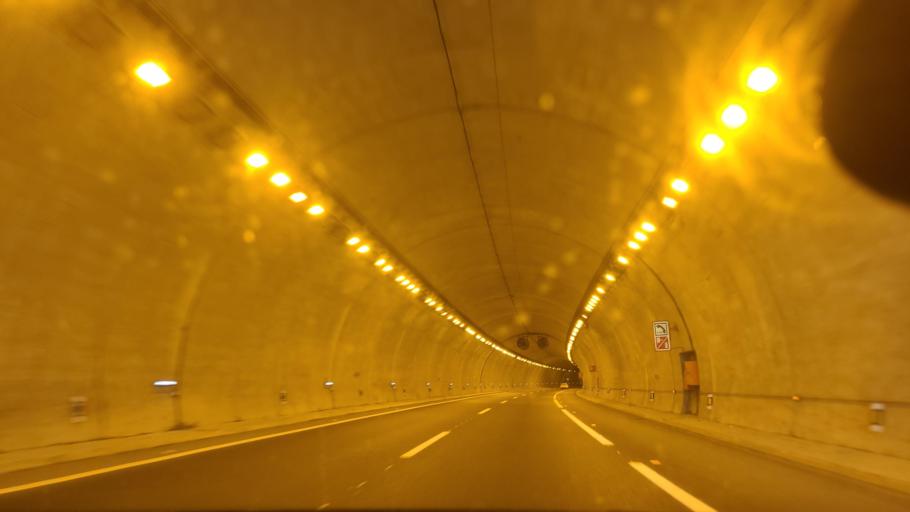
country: ES
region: Andalusia
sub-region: Provincia de Granada
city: Gualchos
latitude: 36.7158
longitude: -3.4518
